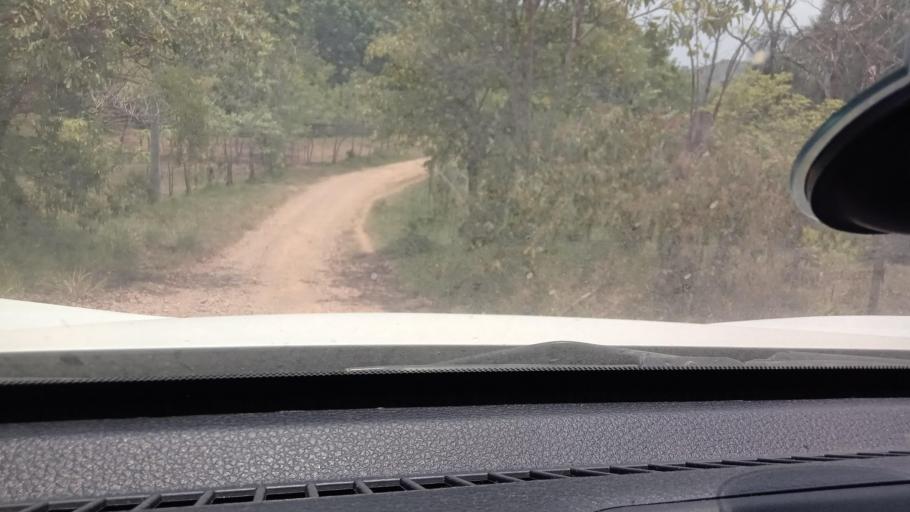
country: MX
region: Tabasco
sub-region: Huimanguillo
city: Francisco Rueda
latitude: 17.4938
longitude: -93.9170
